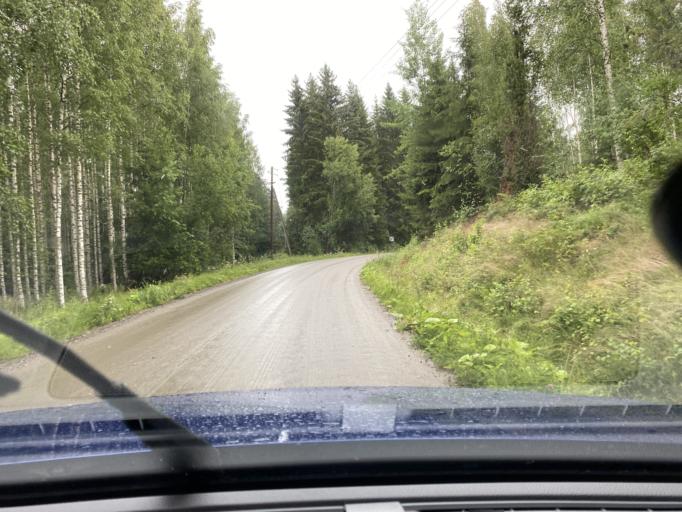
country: FI
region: Pirkanmaa
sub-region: Lounais-Pirkanmaa
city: Punkalaidun
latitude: 61.1484
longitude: 23.1981
